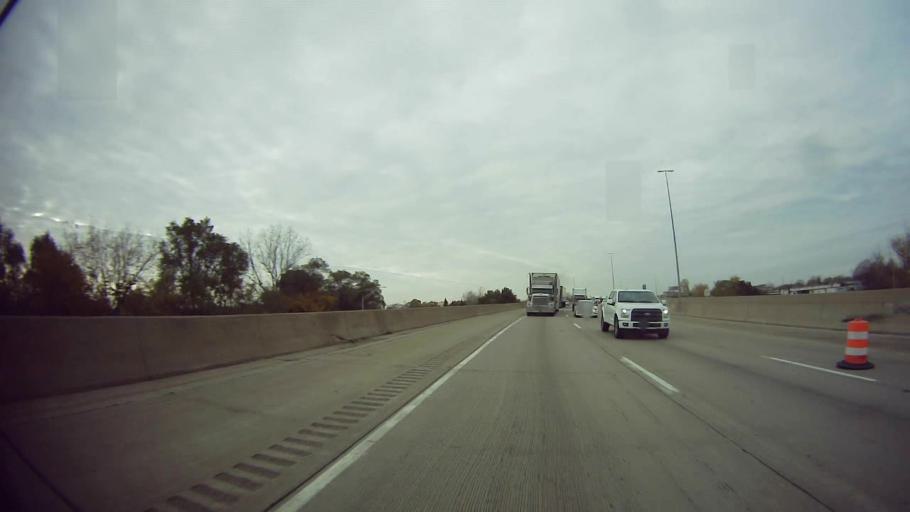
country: US
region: Michigan
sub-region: Wayne County
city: Melvindale
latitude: 42.2659
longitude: -83.1690
